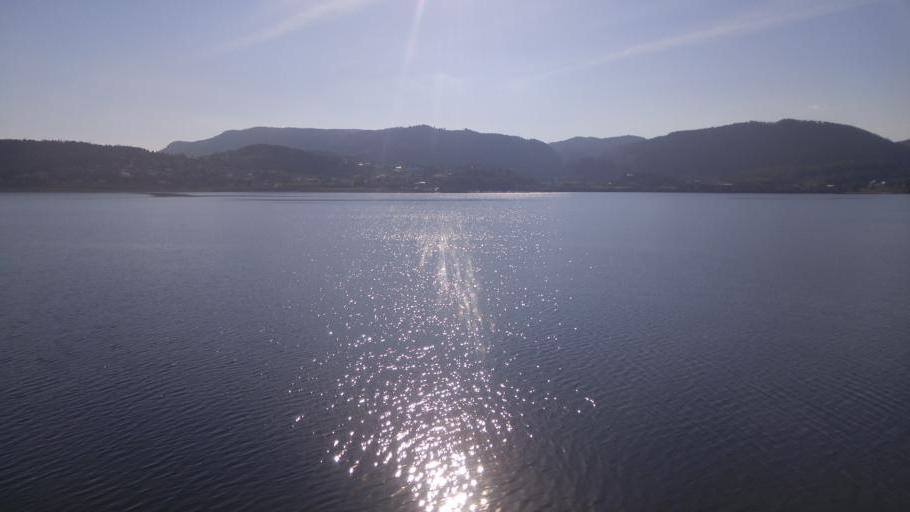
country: NO
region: Sor-Trondelag
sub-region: Malvik
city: Hommelvik
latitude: 63.4205
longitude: 10.7784
